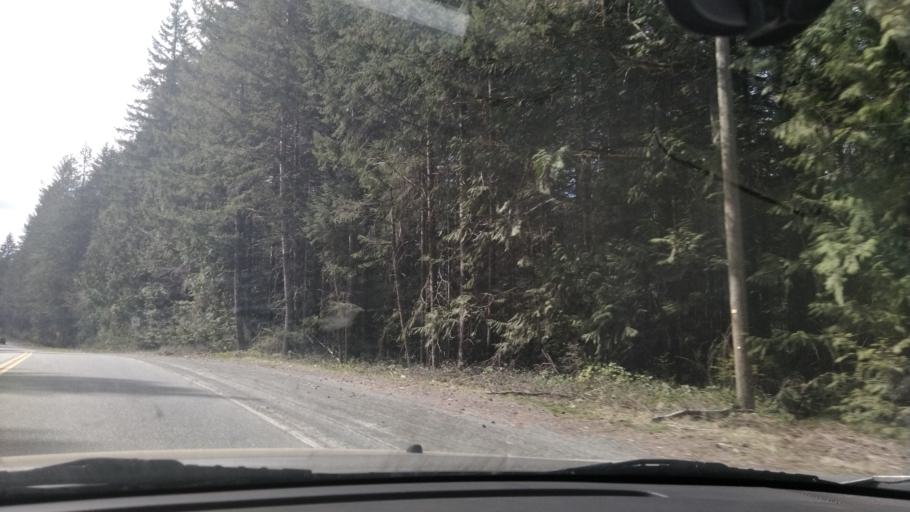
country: CA
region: British Columbia
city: Campbell River
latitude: 49.9829
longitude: -125.4299
